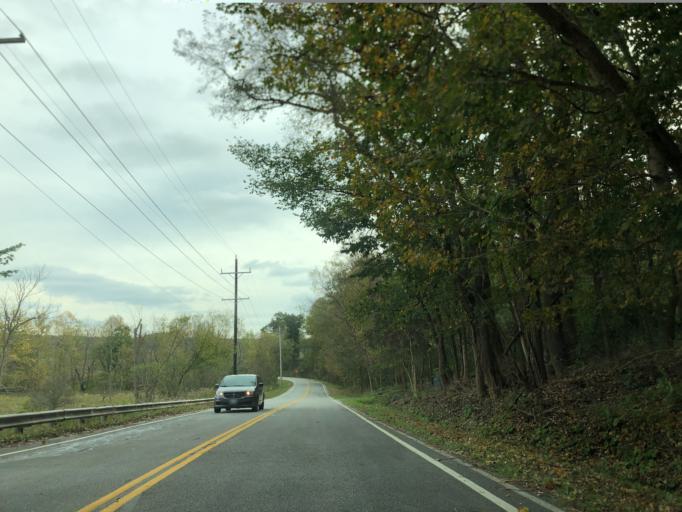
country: US
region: Ohio
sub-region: Summit County
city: Peninsula
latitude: 41.2847
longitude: -81.5779
